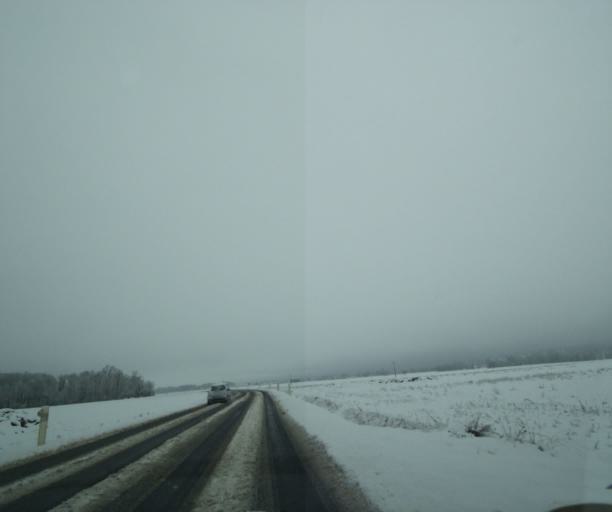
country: FR
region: Champagne-Ardenne
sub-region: Departement de la Haute-Marne
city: Wassy
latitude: 48.5639
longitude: 4.9222
